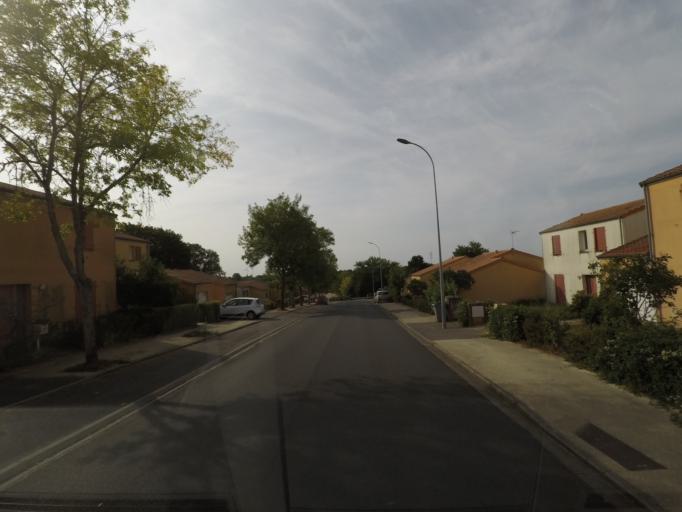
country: FR
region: Poitou-Charentes
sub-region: Departement des Deux-Sevres
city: Melle
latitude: 46.2312
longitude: -0.1377
